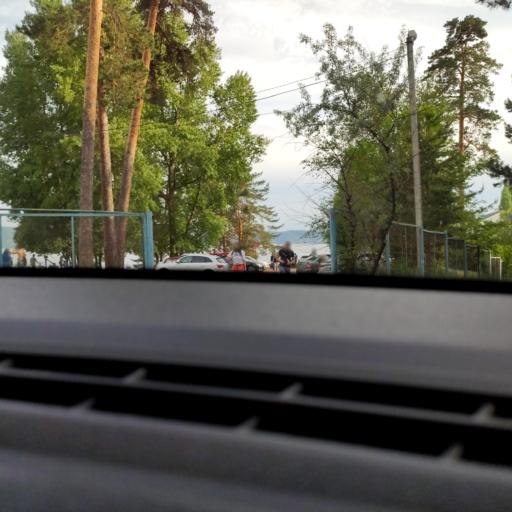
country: RU
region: Samara
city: Tol'yatti
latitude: 53.4742
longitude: 49.3340
